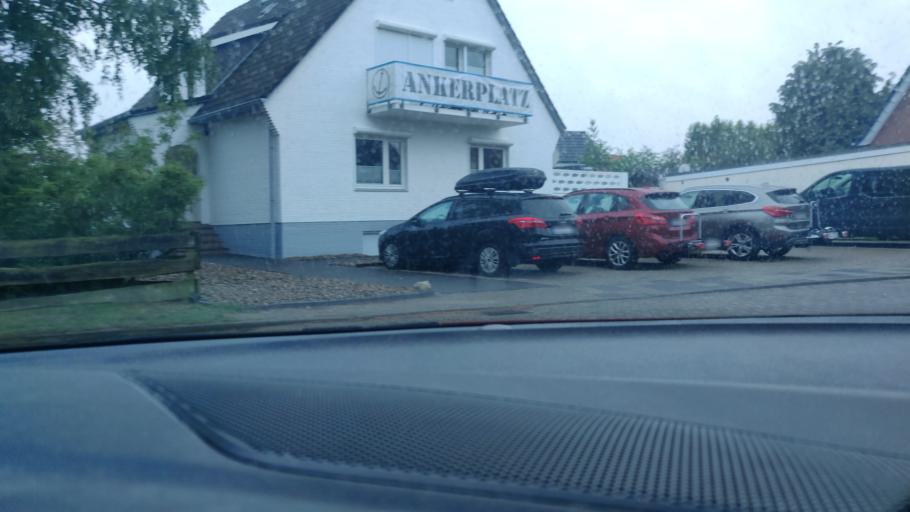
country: DE
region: Lower Saxony
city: Cuxhaven
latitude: 53.8625
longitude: 8.6134
